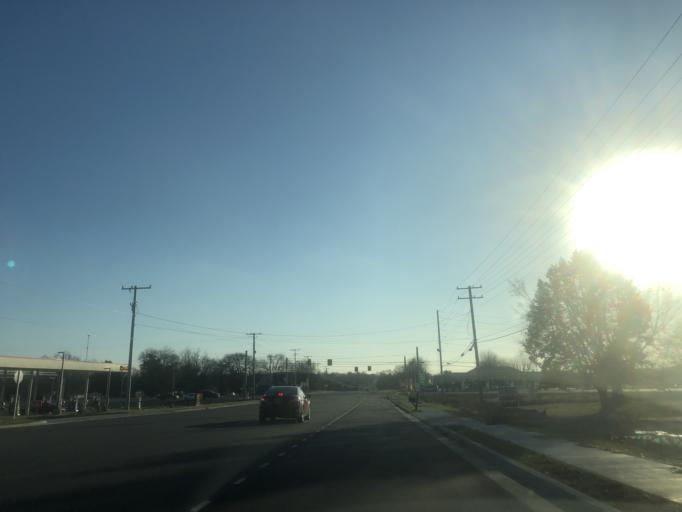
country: US
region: Tennessee
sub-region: Sumner County
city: Portland
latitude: 36.6286
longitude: -86.5669
